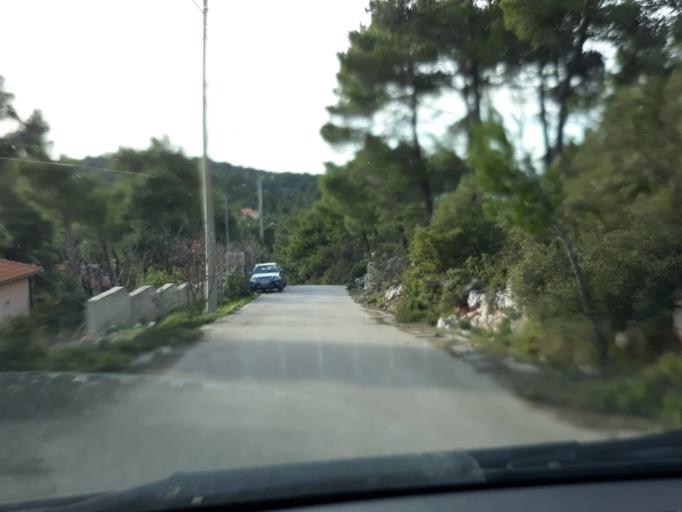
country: GR
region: Attica
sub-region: Nomarchia Anatolikis Attikis
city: Afidnes
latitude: 38.2163
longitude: 23.8032
